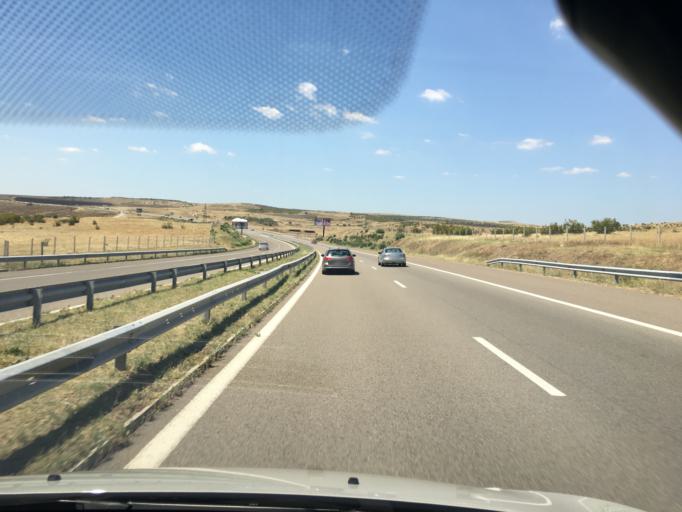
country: BG
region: Burgas
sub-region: Obshtina Kameno
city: Kameno
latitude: 42.5941
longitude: 27.1721
